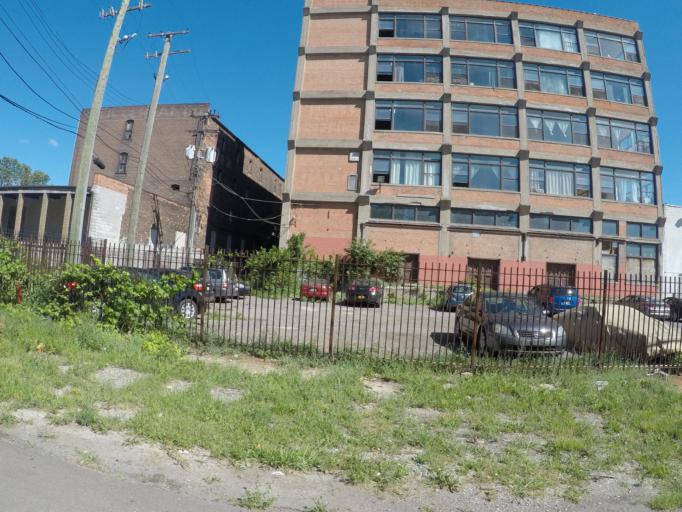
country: US
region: Michigan
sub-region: Wayne County
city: Detroit
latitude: 42.3212
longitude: -83.0669
